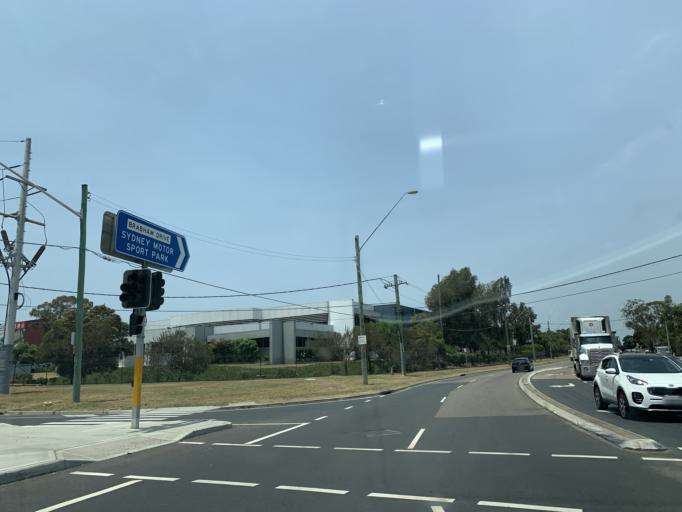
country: AU
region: New South Wales
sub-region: Blacktown
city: Doonside
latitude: -33.7925
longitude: 150.8716
